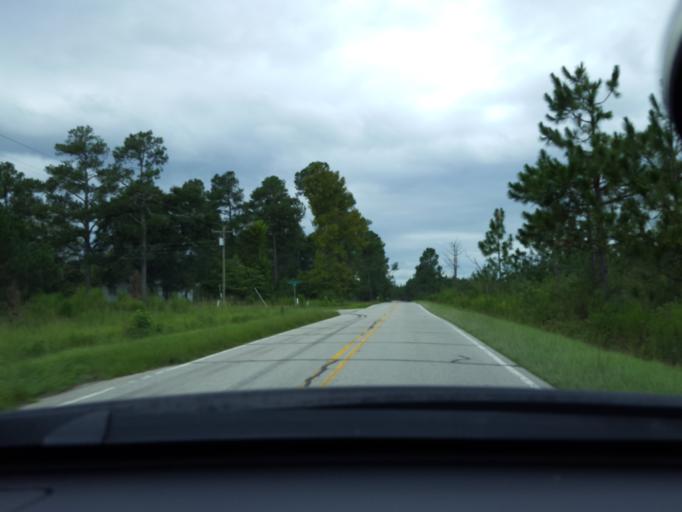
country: US
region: North Carolina
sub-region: Sampson County
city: Clinton
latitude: 34.8005
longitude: -78.2598
